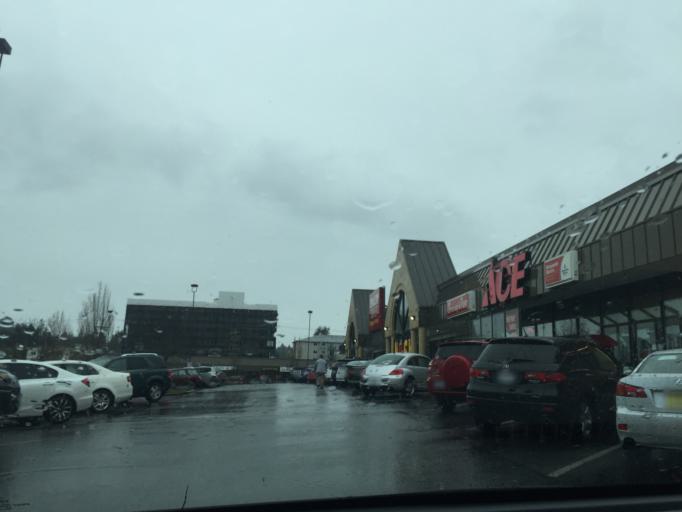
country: US
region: Washington
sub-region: King County
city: Lake Forest Park
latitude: 47.7215
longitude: -122.2945
